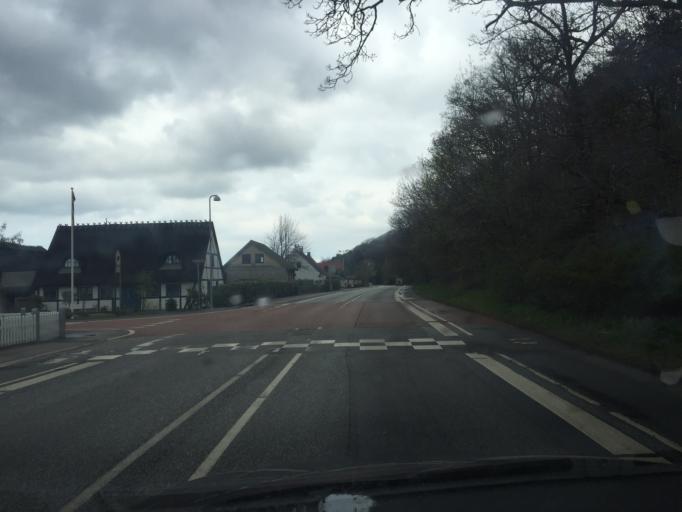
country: DK
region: Capital Region
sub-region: Halsnaes Kommune
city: Frederiksvaerk
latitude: 55.9850
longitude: 12.0190
